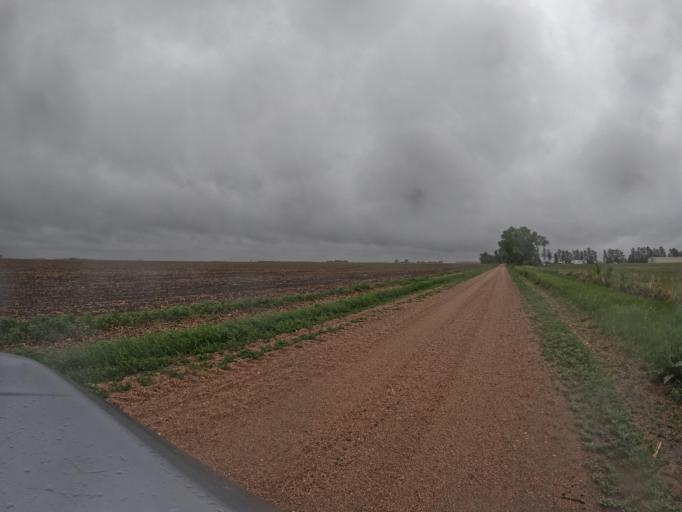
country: US
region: Nebraska
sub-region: Clay County
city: Harvard
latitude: 40.6227
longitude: -98.1040
